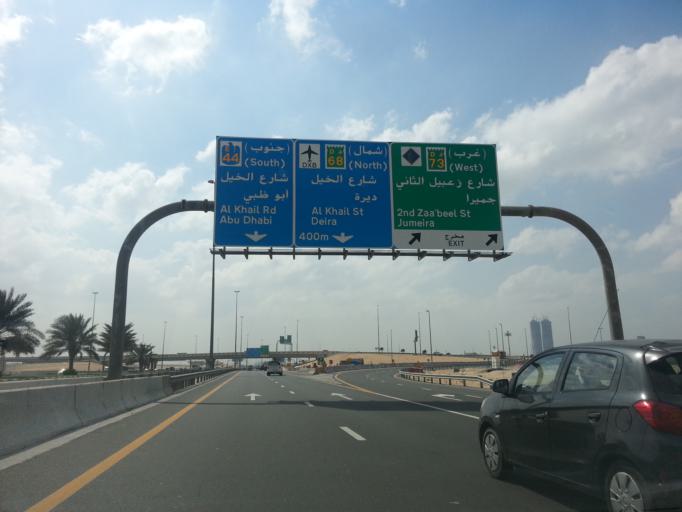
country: AE
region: Ash Shariqah
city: Sharjah
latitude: 25.2117
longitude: 55.3133
